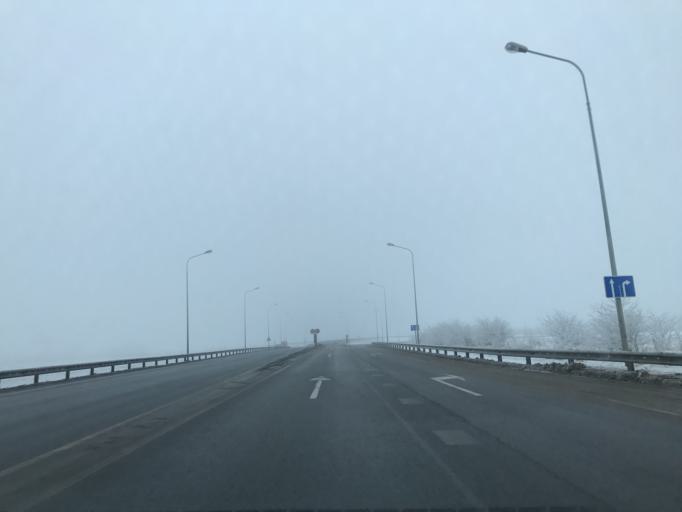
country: RU
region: Rostov
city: Grushevskaya
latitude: 47.3788
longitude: 39.9001
